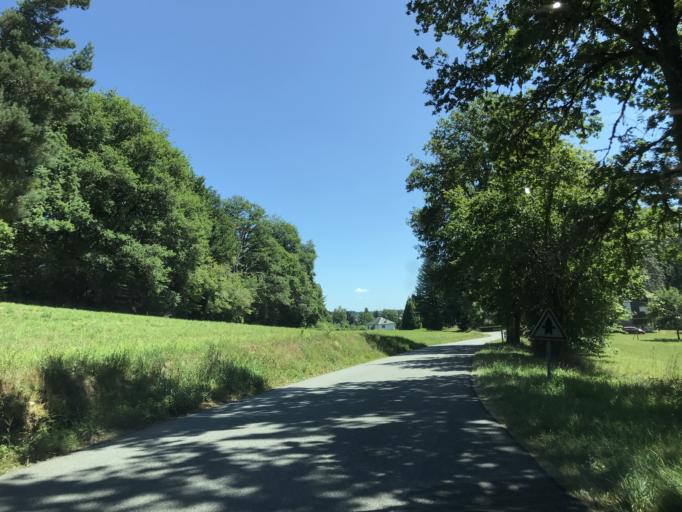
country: FR
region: Limousin
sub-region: Departement de la Correze
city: Neuvic
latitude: 45.3763
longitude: 2.2621
